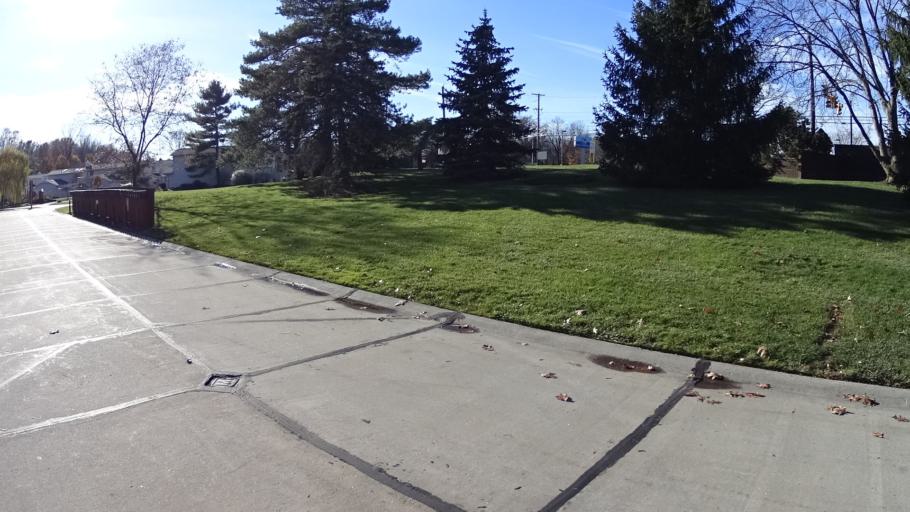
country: US
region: Ohio
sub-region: Lorain County
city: North Ridgeville
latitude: 41.4068
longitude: -81.9800
